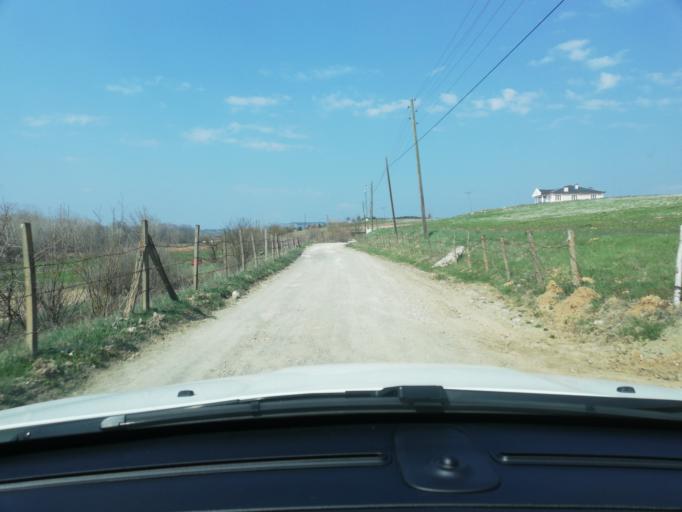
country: TR
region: Kastamonu
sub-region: Cide
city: Kastamonu
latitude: 41.4602
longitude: 33.7555
